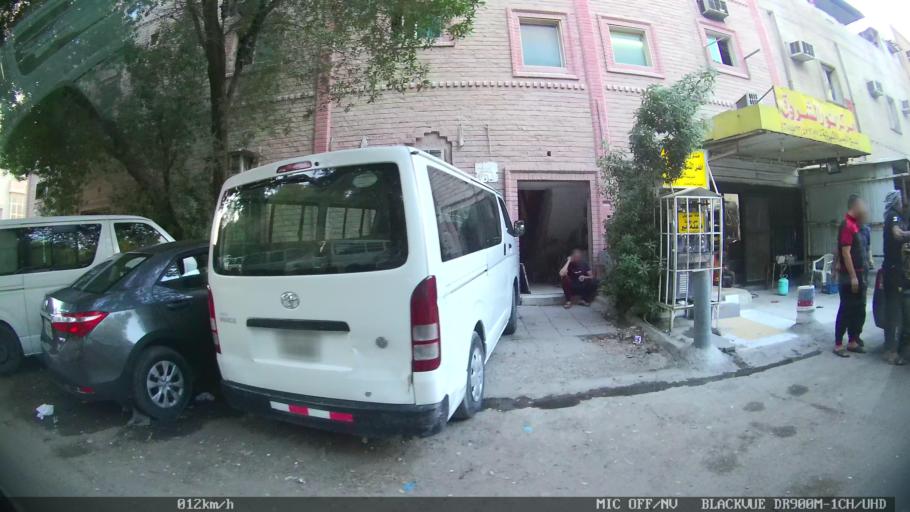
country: KW
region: Al Farwaniyah
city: Janub as Surrah
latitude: 29.2910
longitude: 47.9780
